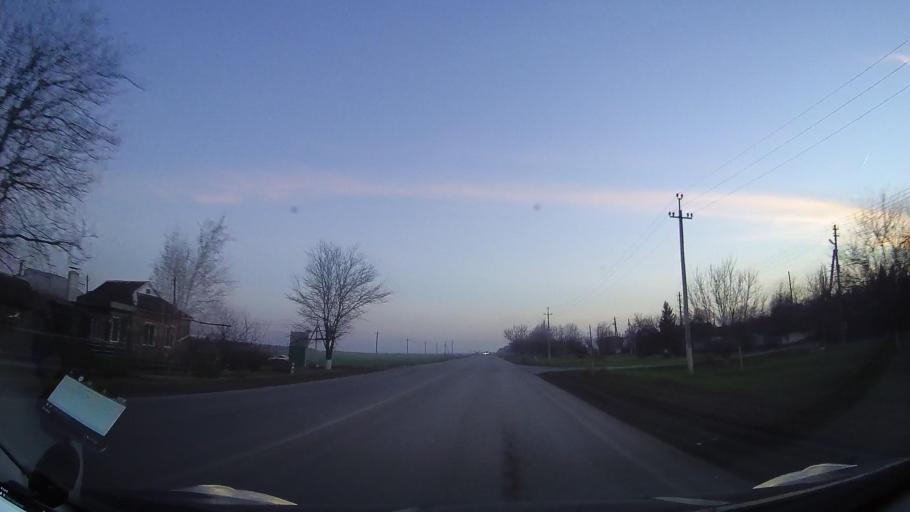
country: RU
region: Rostov
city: Zernograd
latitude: 46.8358
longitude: 40.2994
